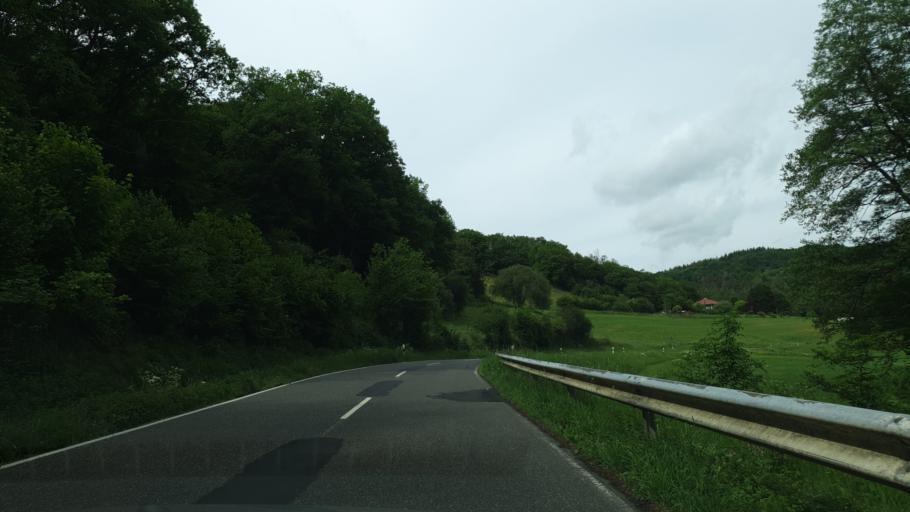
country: DE
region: Rheinland-Pfalz
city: Gackenbach
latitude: 50.3482
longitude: 7.8635
